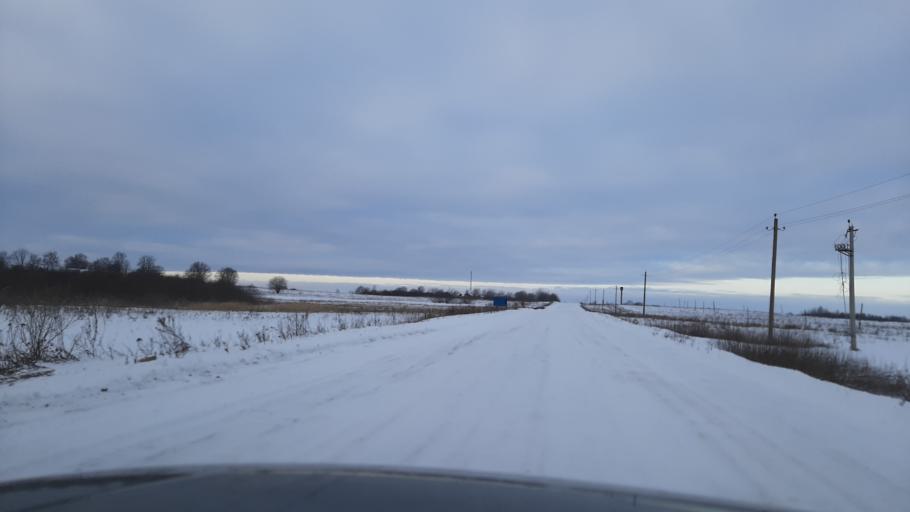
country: RU
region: Kostroma
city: Kosmynino
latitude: 57.4458
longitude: 40.9252
